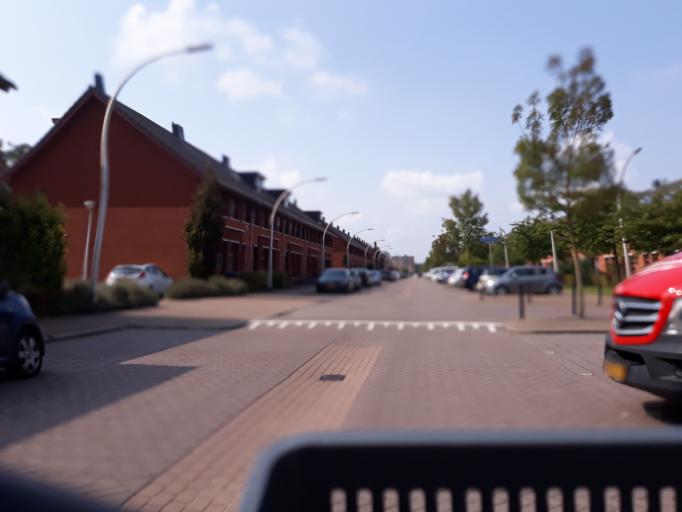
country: NL
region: South Holland
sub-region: Gemeente Hendrik-Ido-Ambacht
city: Hendrik-Ido-Ambacht
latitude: 51.8310
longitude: 4.6586
